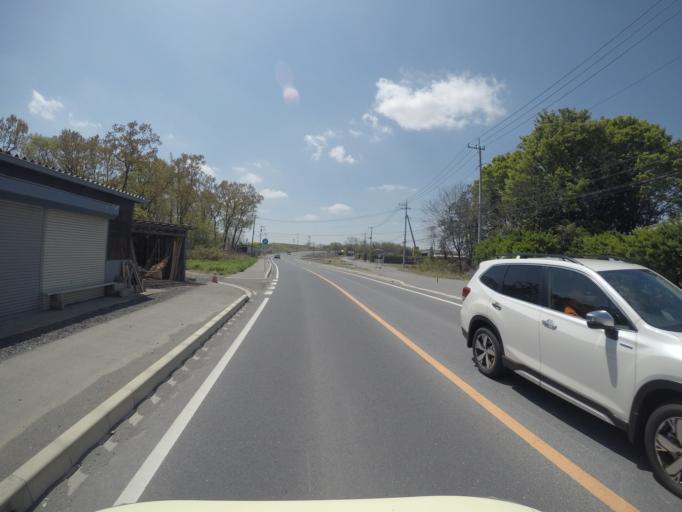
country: JP
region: Tochigi
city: Mibu
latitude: 36.3918
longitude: 139.7991
